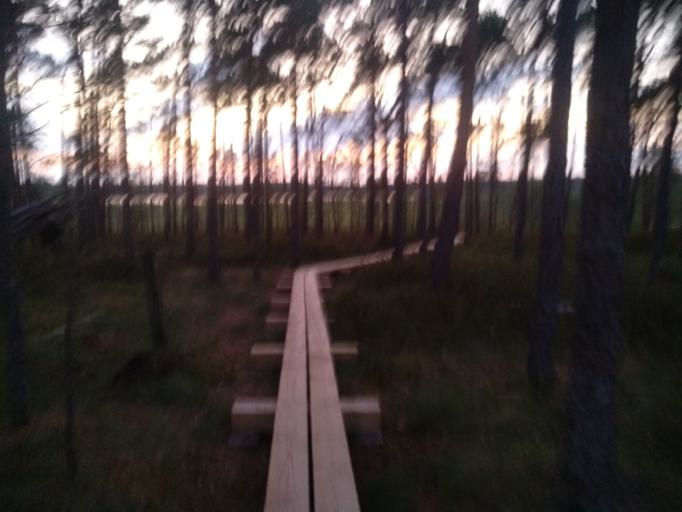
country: EE
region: Jaervamaa
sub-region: Paide linn
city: Paide
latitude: 59.0806
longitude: 25.5217
